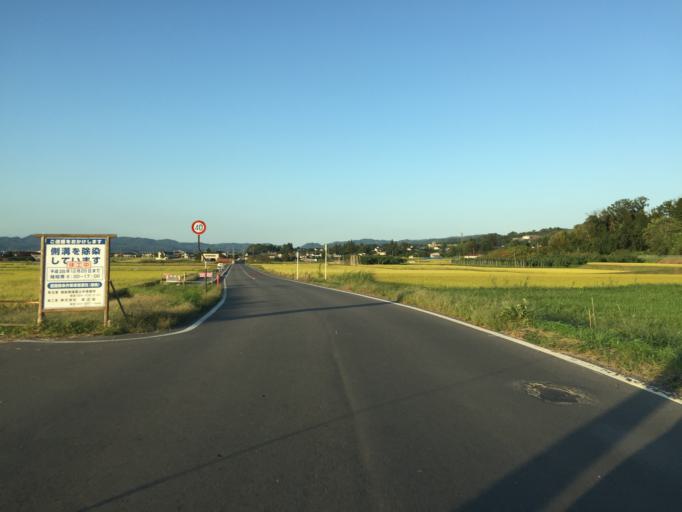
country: JP
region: Fukushima
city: Yanagawamachi-saiwaicho
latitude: 37.8228
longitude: 140.5895
